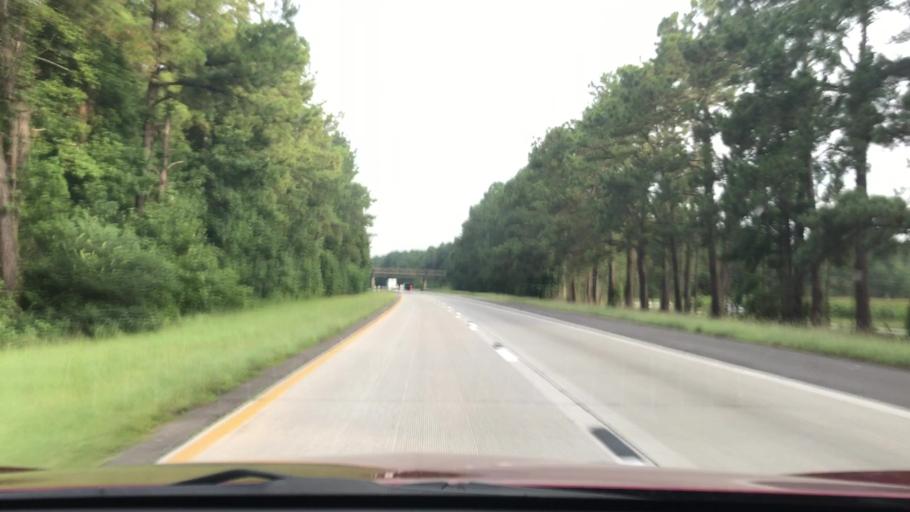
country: US
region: South Carolina
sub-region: Orangeburg County
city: Holly Hill
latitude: 33.2220
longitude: -80.4237
